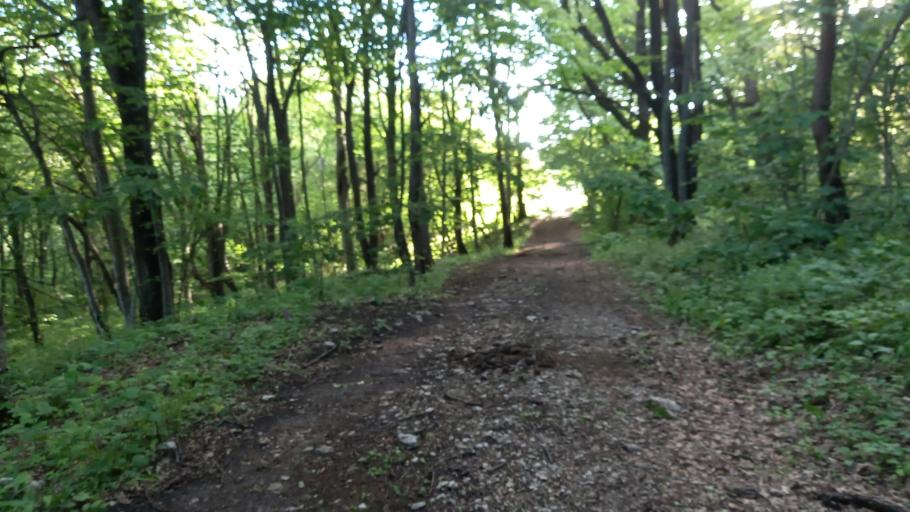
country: RU
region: Adygeya
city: Kamennomostskiy
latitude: 44.2194
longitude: 40.0048
